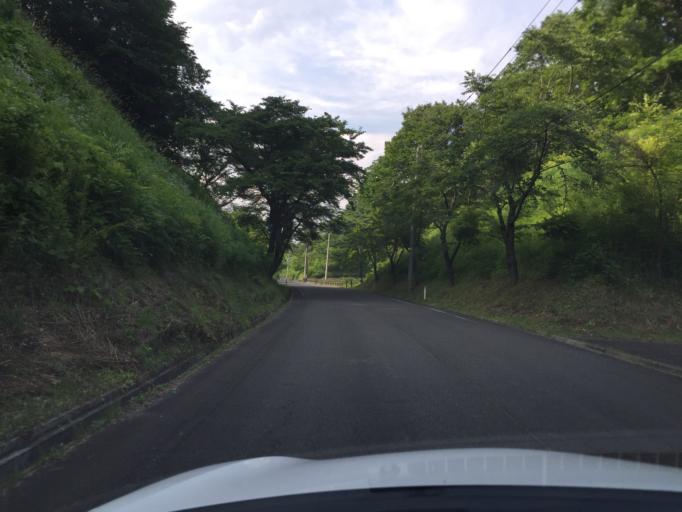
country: JP
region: Fukushima
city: Miharu
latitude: 37.3999
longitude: 140.4793
